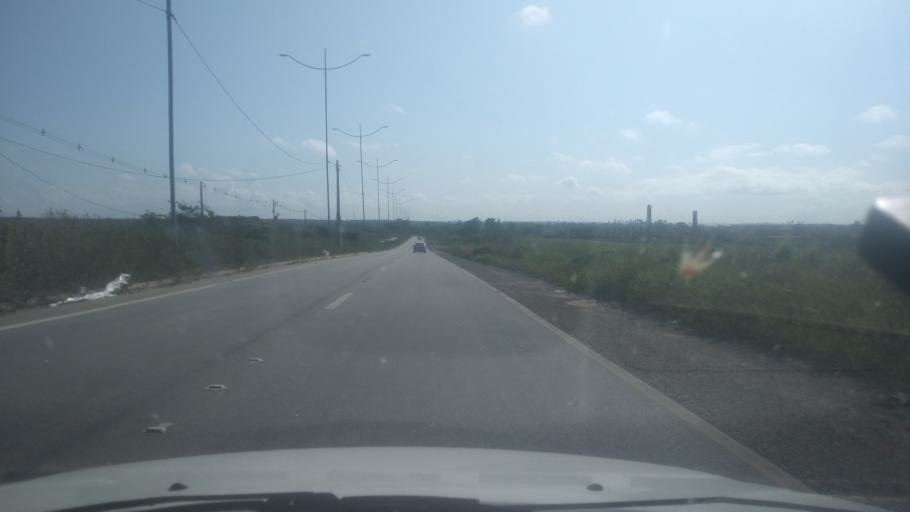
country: BR
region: Rio Grande do Norte
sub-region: Macaiba
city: Macaiba
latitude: -5.8187
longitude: -35.3652
